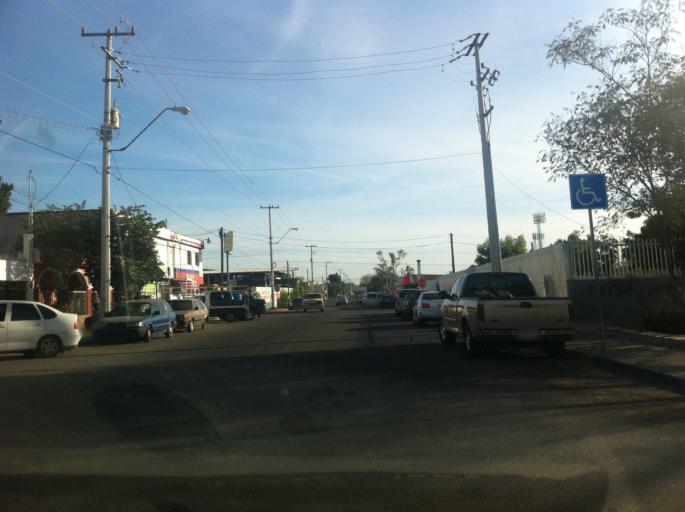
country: MX
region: Sonora
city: Hermosillo
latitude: 29.0999
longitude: -110.9899
